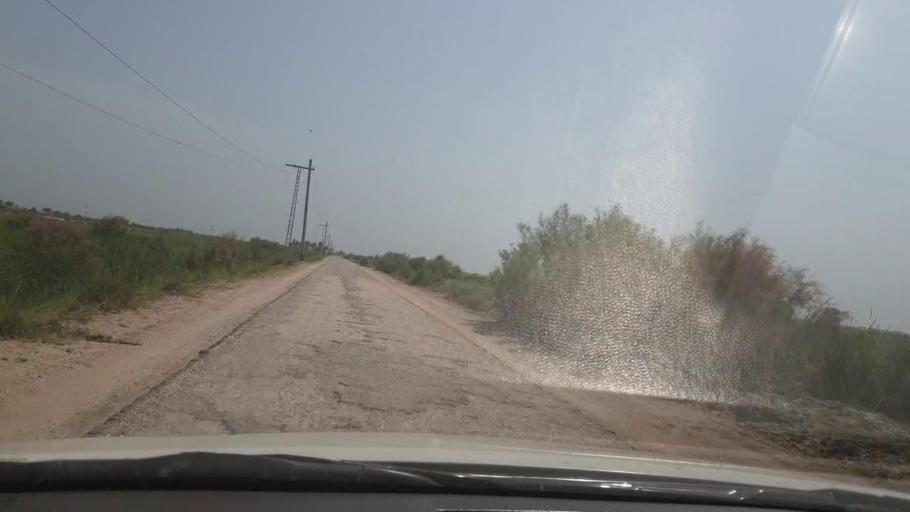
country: PK
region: Sindh
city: Garhi Yasin
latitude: 27.9644
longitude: 68.5044
